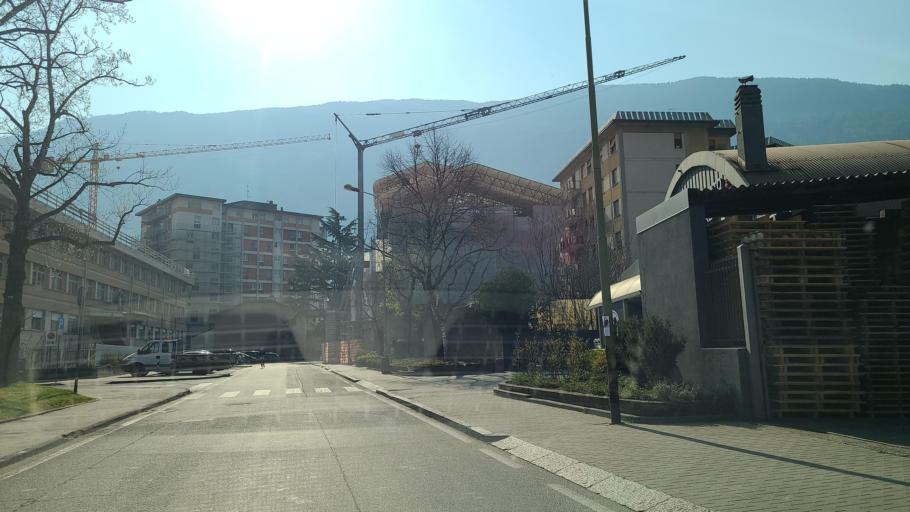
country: IT
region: Lombardy
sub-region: Provincia di Sondrio
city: Tirano
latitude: 46.2178
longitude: 10.1648
